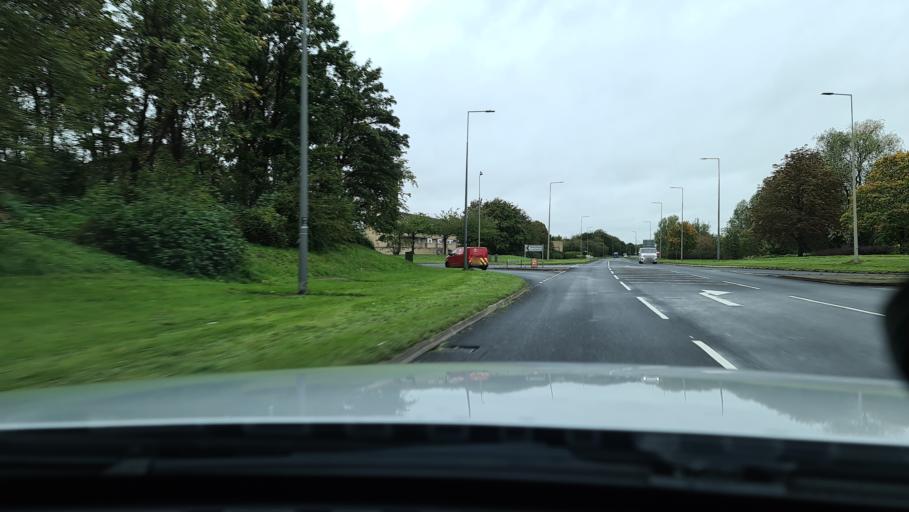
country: GB
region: England
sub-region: Milton Keynes
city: Bradwell
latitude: 52.0533
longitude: -0.8148
